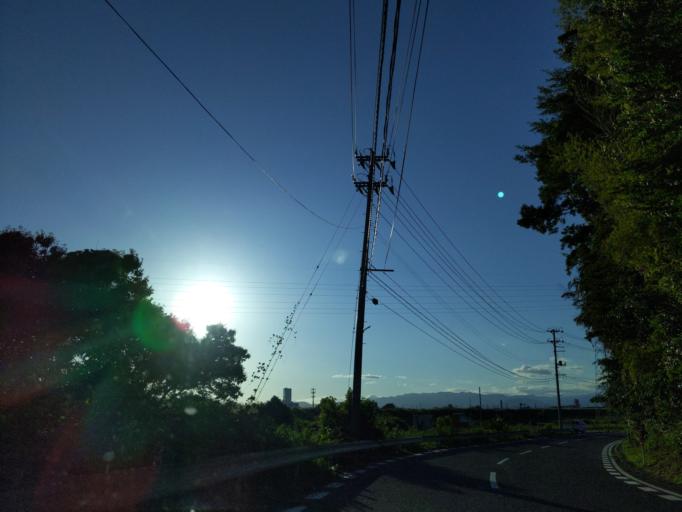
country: JP
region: Fukushima
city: Koriyama
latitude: 37.3886
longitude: 140.4124
